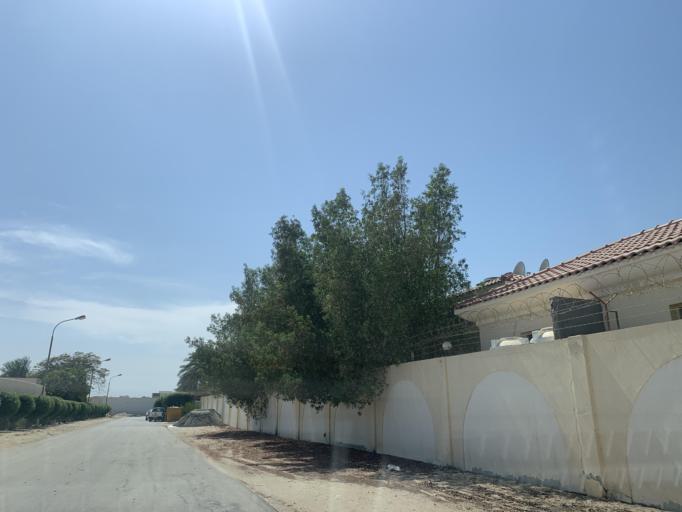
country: BH
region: Central Governorate
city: Madinat Hamad
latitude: 26.1783
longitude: 50.4712
